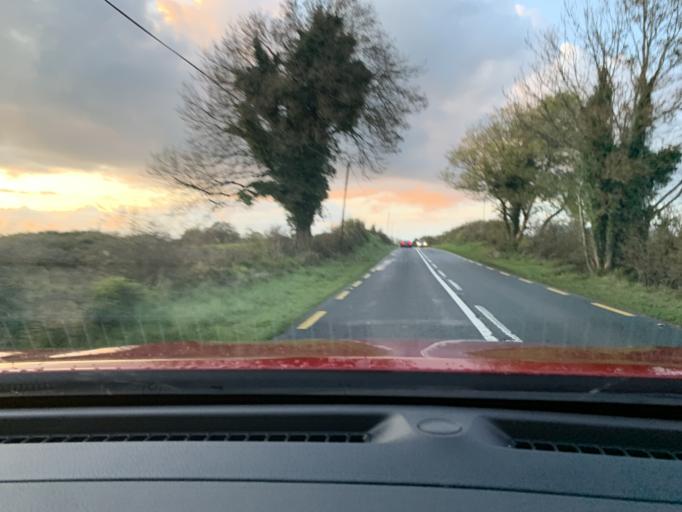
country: IE
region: Connaught
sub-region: Sligo
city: Ballymote
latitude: 54.1089
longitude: -8.4162
